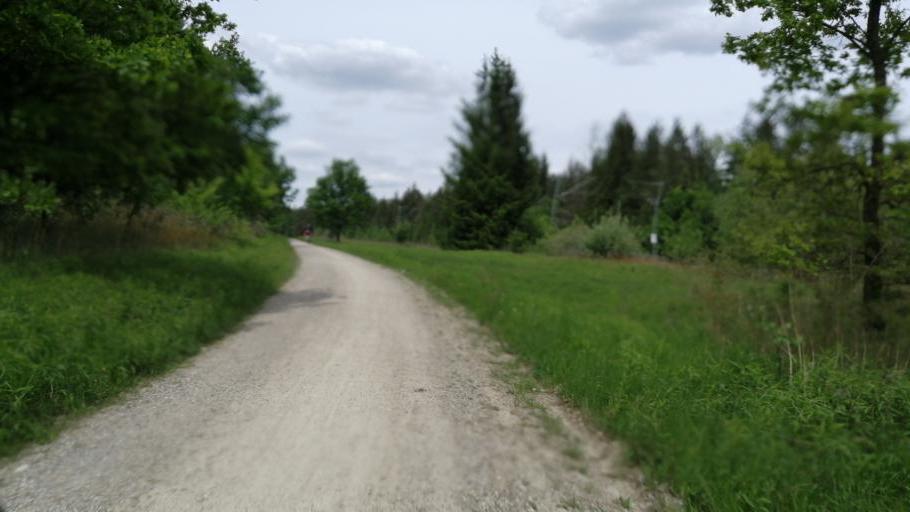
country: DE
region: Bavaria
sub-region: Upper Bavaria
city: Pullach im Isartal
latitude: 48.0637
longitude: 11.5623
